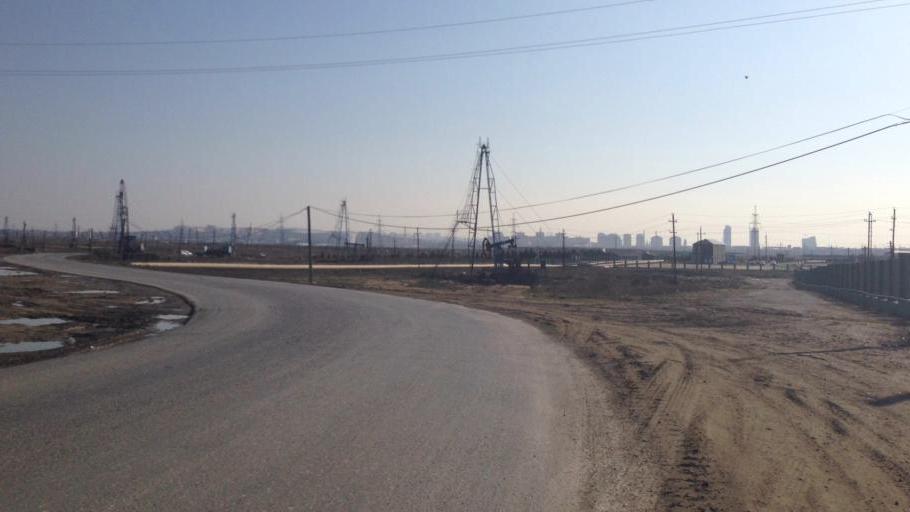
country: AZ
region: Baki
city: Balakhani
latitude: 40.4574
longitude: 49.8915
